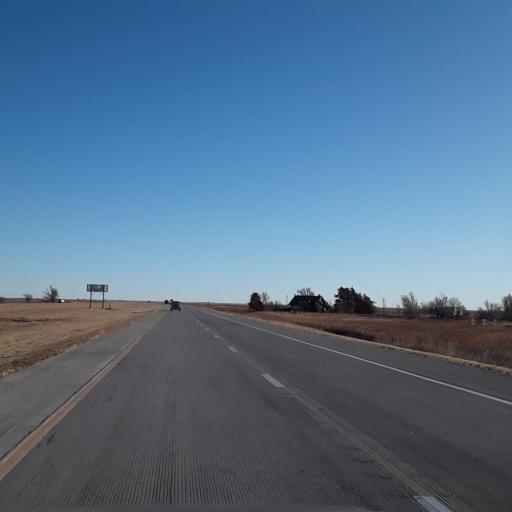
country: US
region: Kansas
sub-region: Seward County
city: Liberal
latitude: 37.0973
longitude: -100.8080
